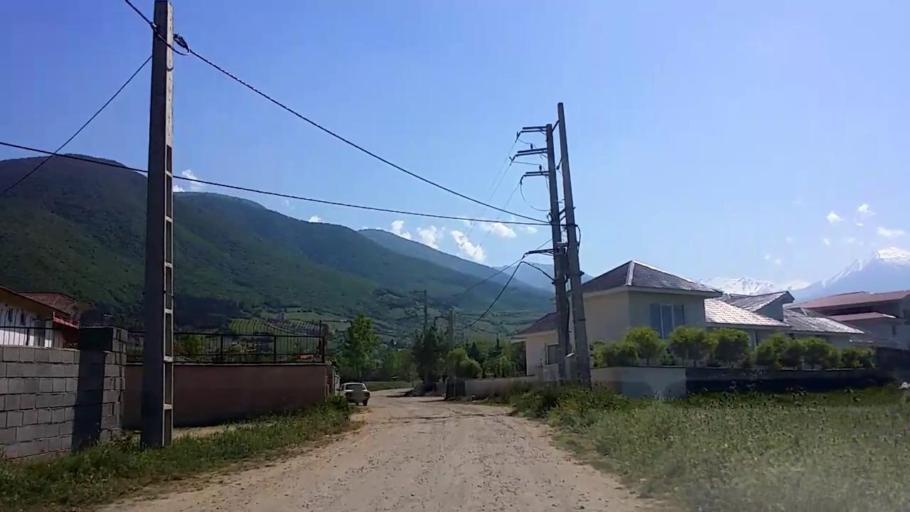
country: IR
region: Mazandaran
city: `Abbasabad
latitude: 36.5112
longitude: 51.1974
